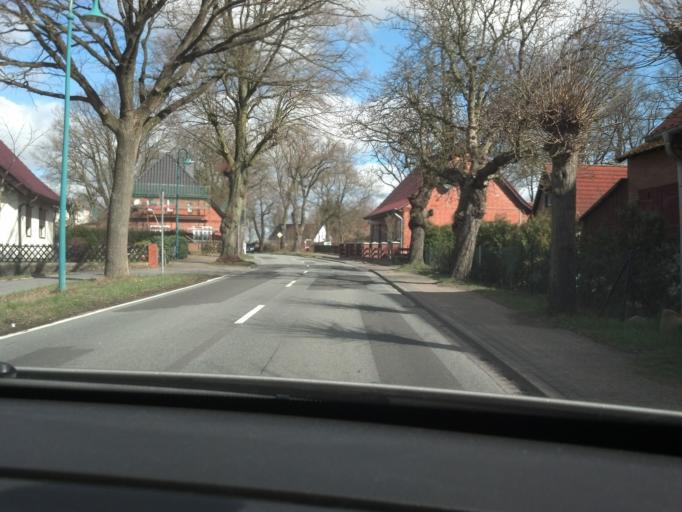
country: DE
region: Schleswig-Holstein
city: Gudow
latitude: 53.4901
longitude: 10.8319
